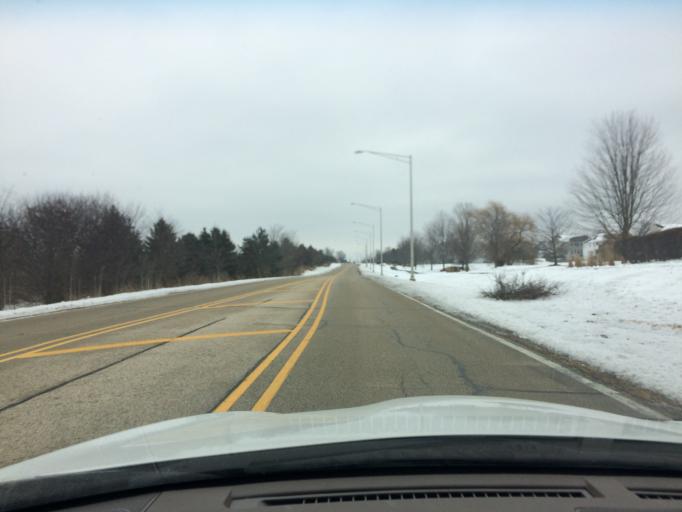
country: US
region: Illinois
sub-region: Kane County
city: Saint Charles
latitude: 41.8975
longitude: -88.3545
